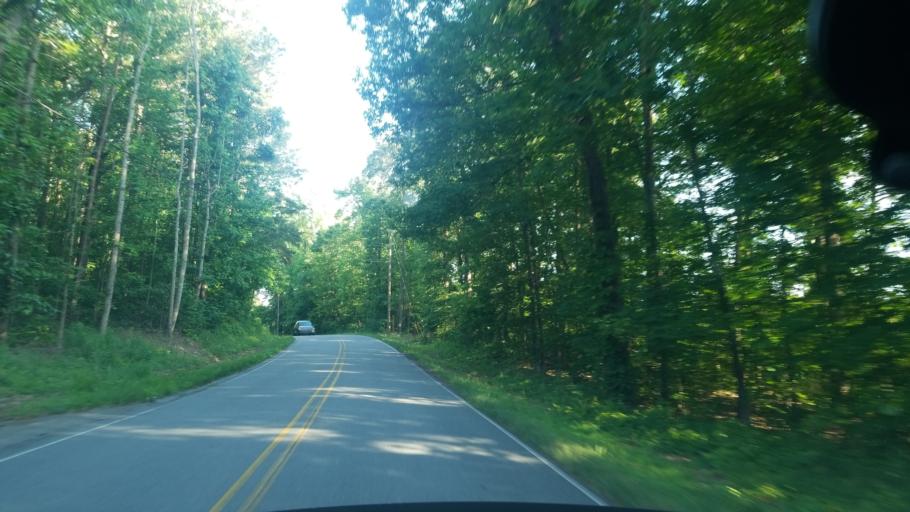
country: US
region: Georgia
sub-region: Fulton County
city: Johns Creek
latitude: 34.0906
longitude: -84.1621
